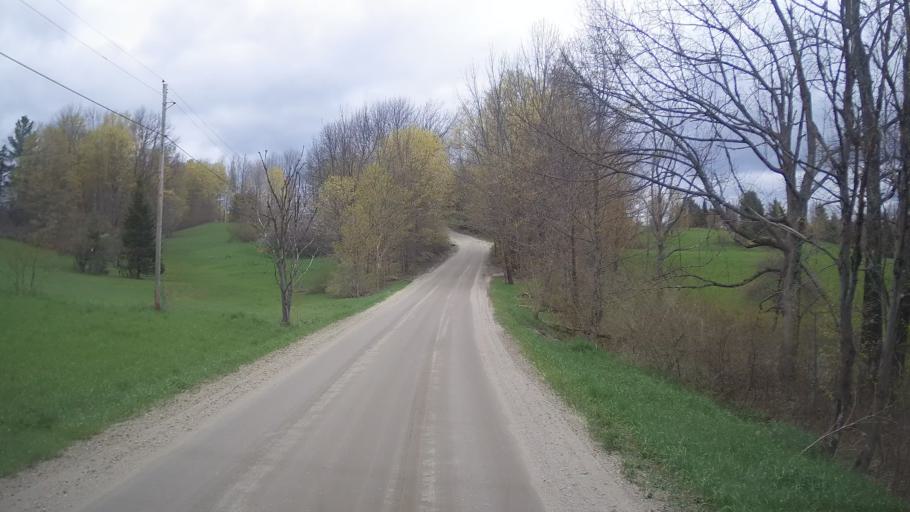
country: US
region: Vermont
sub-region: Caledonia County
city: Lyndonville
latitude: 44.6054
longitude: -71.9496
